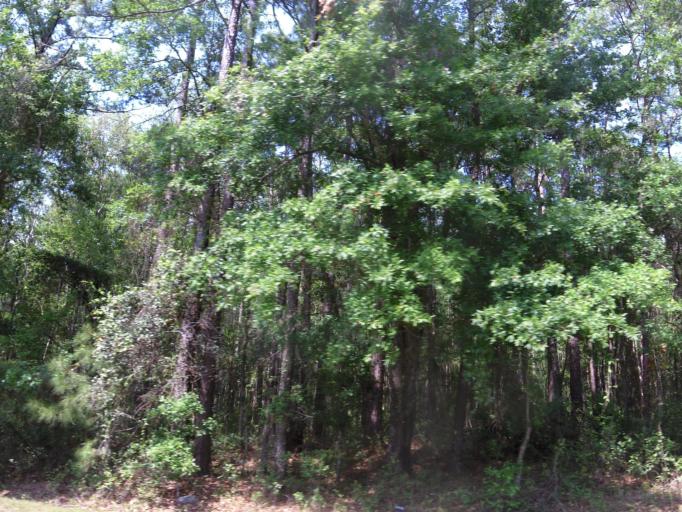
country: US
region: Georgia
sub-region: Camden County
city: Kingsland
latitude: 30.8042
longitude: -81.7401
